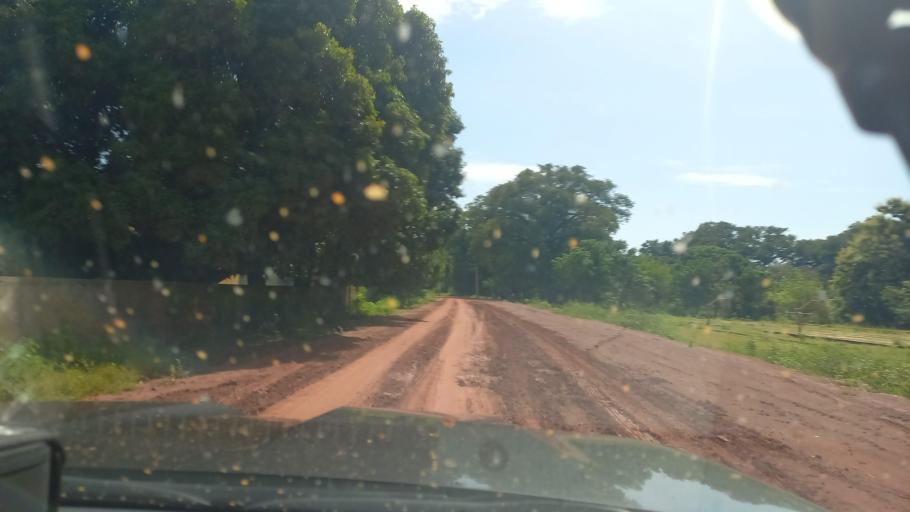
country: SN
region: Ziguinchor
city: Adeane
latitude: 12.6690
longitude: -16.0916
